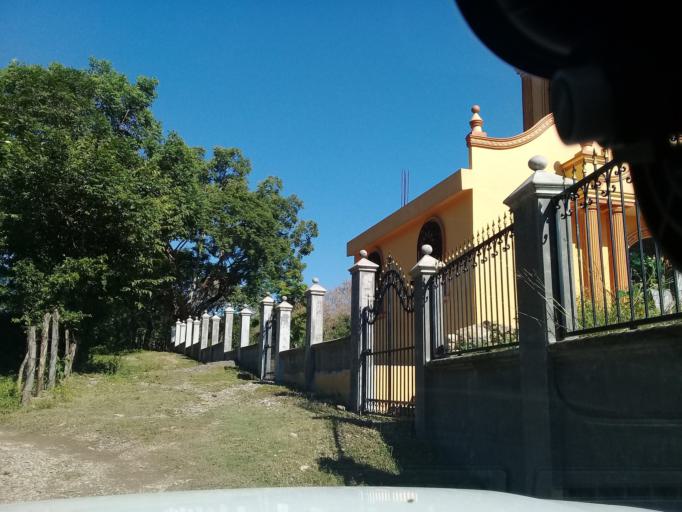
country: MX
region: Hidalgo
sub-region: Huejutla de Reyes
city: Huejutla de Reyes
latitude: 21.1617
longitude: -98.4144
